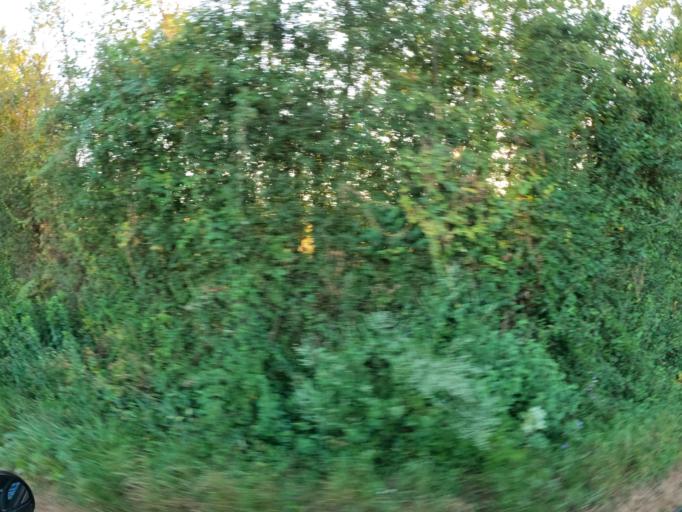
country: FR
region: Pays de la Loire
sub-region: Departement de la Sarthe
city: Parce-sur-Sarthe
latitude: 47.8977
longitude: -0.2186
